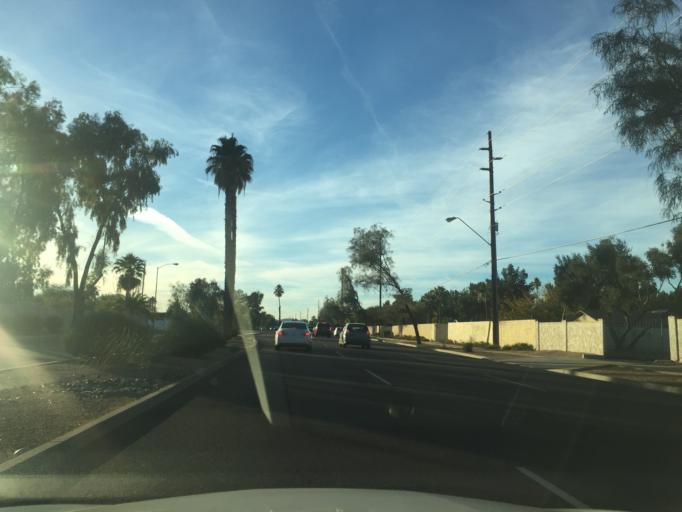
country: US
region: Arizona
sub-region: Maricopa County
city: Paradise Valley
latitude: 33.5826
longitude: -111.9573
